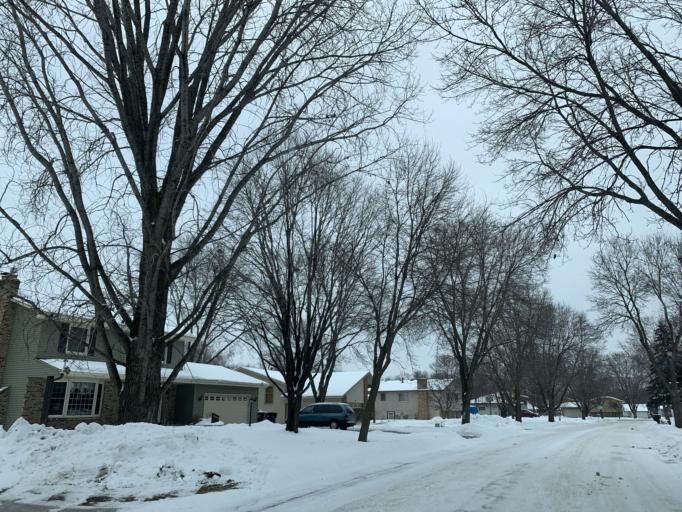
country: US
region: Minnesota
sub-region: Anoka County
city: Coon Rapids
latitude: 45.1604
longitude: -93.3025
